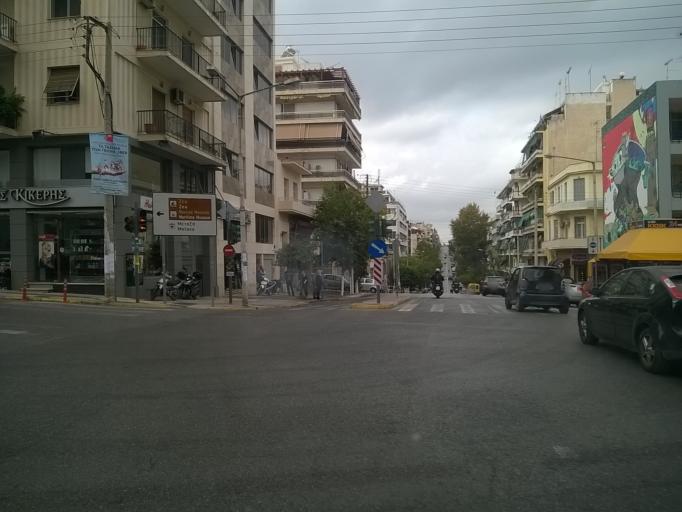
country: GR
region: Attica
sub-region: Nomos Attikis
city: Piraeus
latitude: 37.9364
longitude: 23.6412
